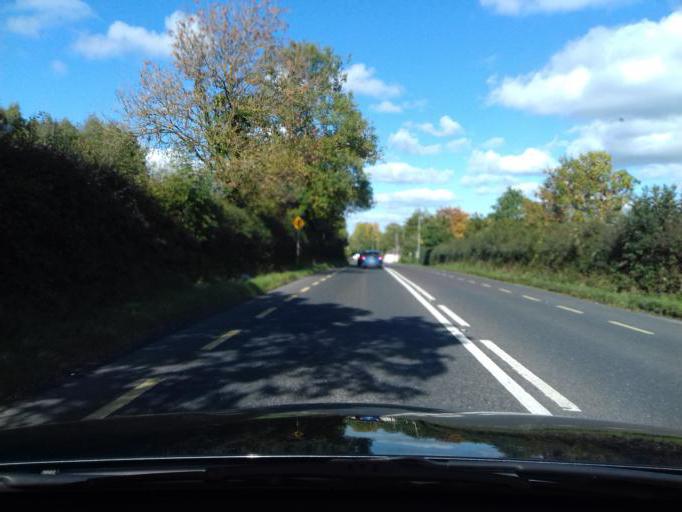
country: IE
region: Leinster
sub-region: An Mhi
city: Ratoath
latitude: 53.5697
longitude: -6.4475
